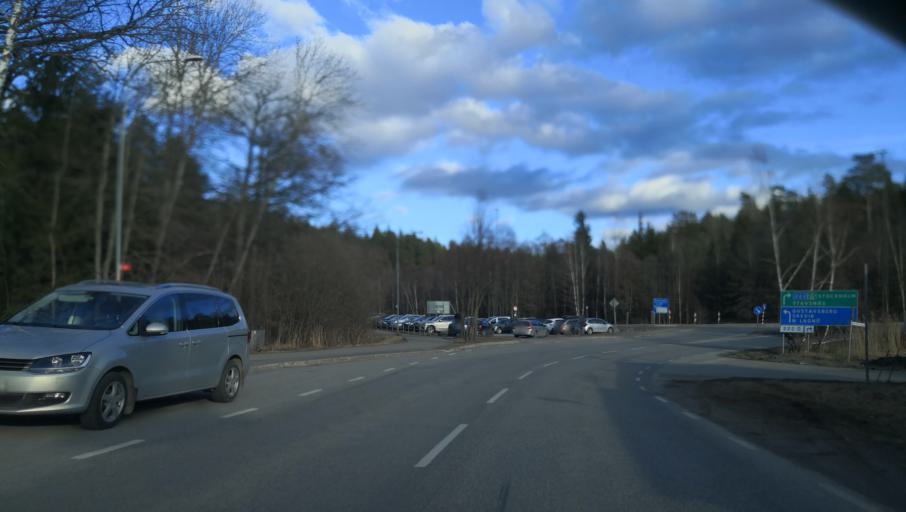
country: SE
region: Stockholm
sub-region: Varmdo Kommun
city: Gustavsberg
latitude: 59.3313
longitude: 18.3432
